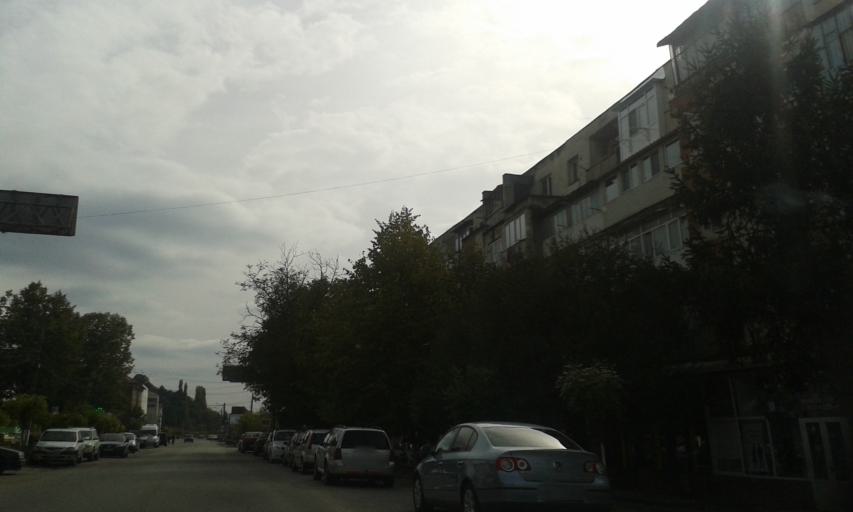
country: RO
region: Gorj
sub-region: Comuna Targu Carbunesti
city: Targu Carbunesti
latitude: 44.9627
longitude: 23.5078
